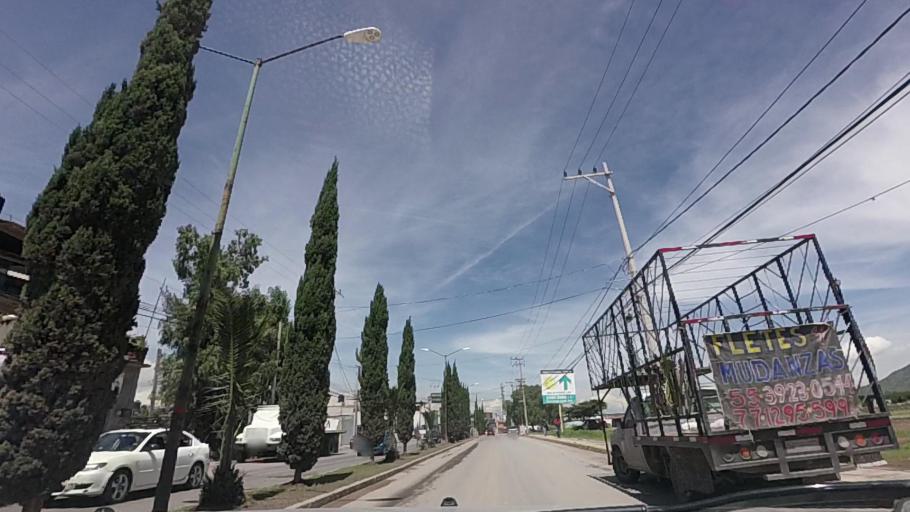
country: MX
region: Mexico
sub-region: Huehuetoca
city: Casa Nueva
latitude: 19.8316
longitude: -99.2121
